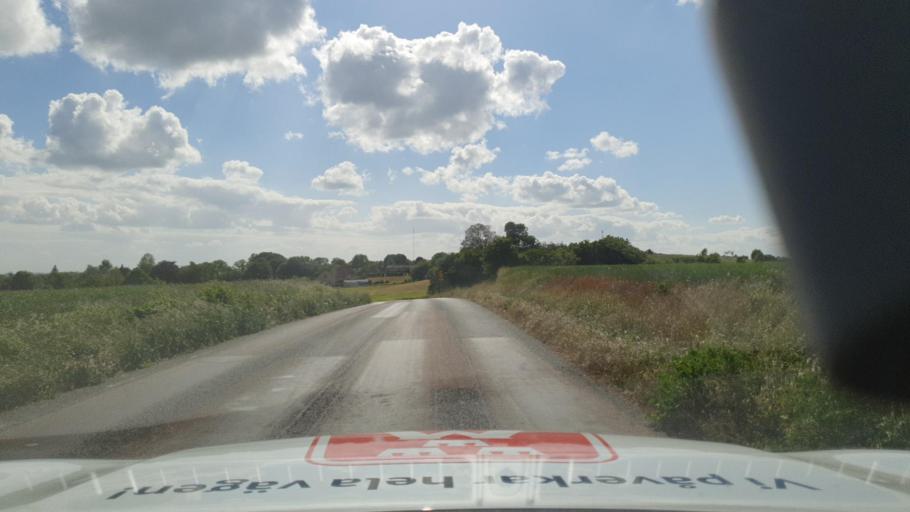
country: SE
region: Skane
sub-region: Simrishamns Kommun
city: Simrishamn
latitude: 55.5631
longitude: 14.2965
